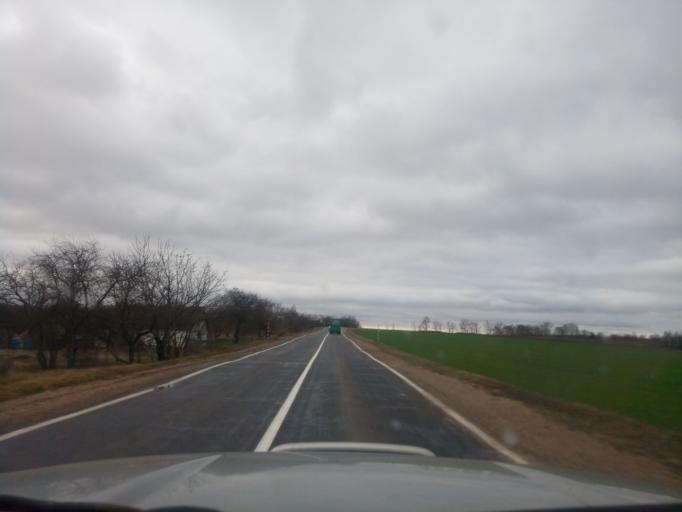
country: BY
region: Minsk
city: Kapyl'
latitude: 53.1746
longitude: 27.1631
